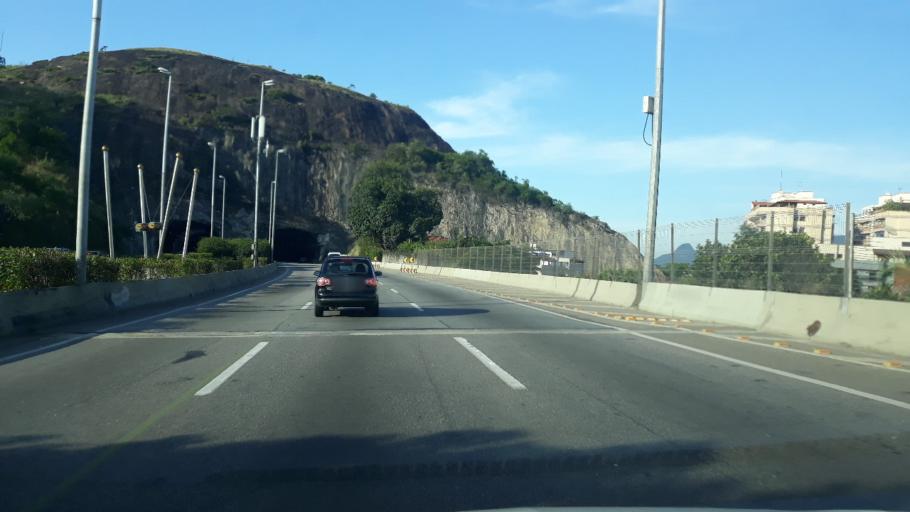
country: BR
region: Rio de Janeiro
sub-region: Sao Joao De Meriti
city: Sao Joao de Meriti
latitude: -22.9277
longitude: -43.3424
